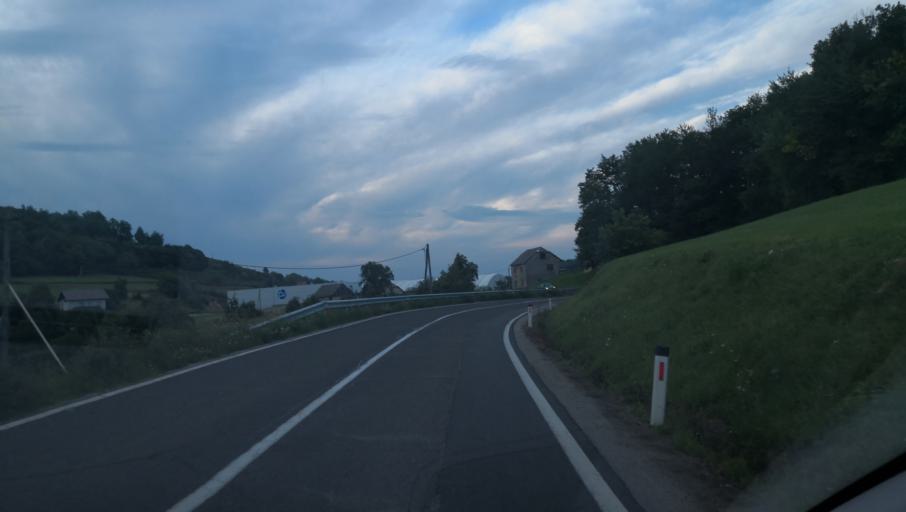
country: SI
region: Metlika
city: Metlika
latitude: 45.6849
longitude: 15.2771
